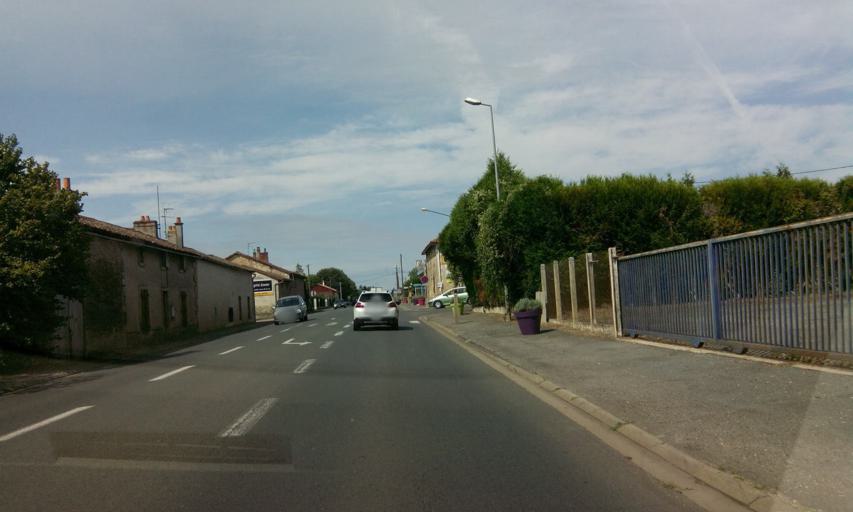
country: FR
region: Poitou-Charentes
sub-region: Departement des Deux-Sevres
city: Sauze-Vaussais
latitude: 46.1341
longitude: 0.1175
